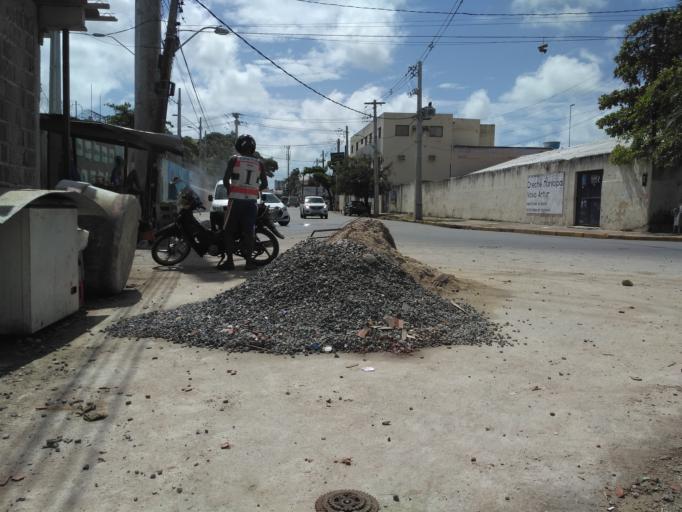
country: BR
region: Pernambuco
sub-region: Recife
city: Recife
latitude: -8.0693
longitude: -34.8914
